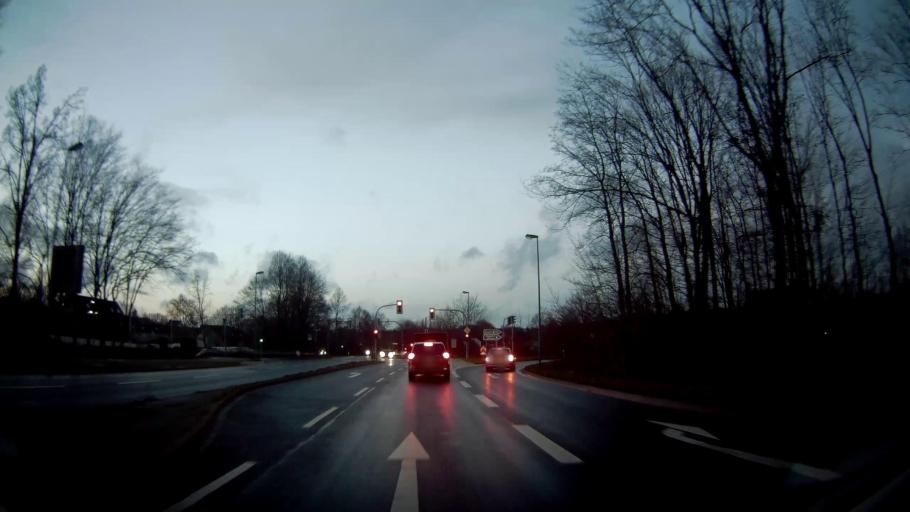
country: DE
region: North Rhine-Westphalia
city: Castrop-Rauxel
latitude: 51.4971
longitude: 7.2894
